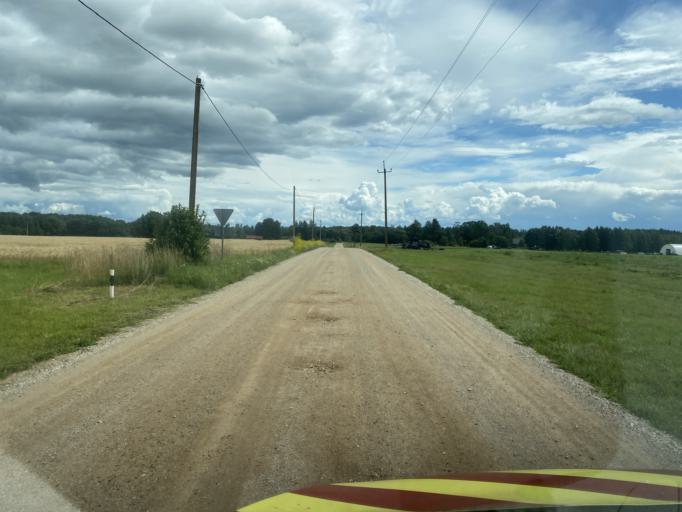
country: EE
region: Valgamaa
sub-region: Torva linn
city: Torva
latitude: 57.9675
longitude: 25.9662
